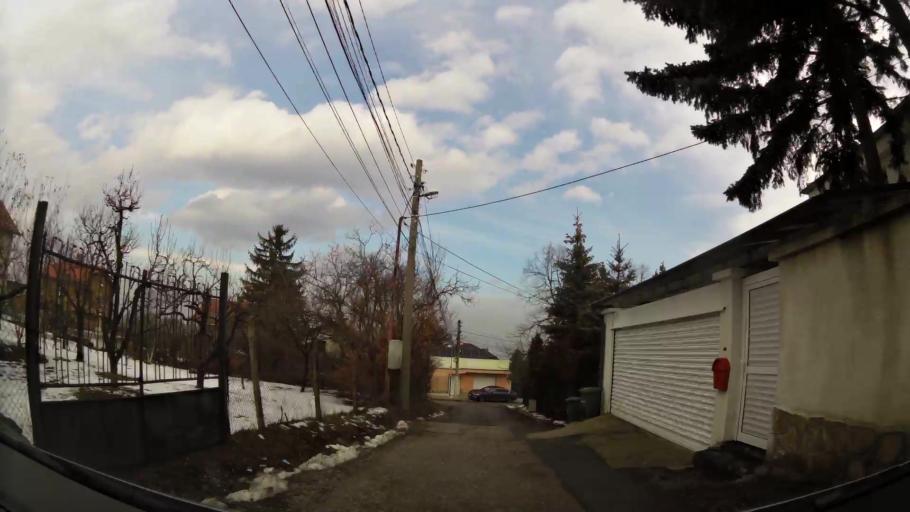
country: BG
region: Sofia-Capital
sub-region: Stolichna Obshtina
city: Sofia
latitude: 42.6463
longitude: 23.2795
